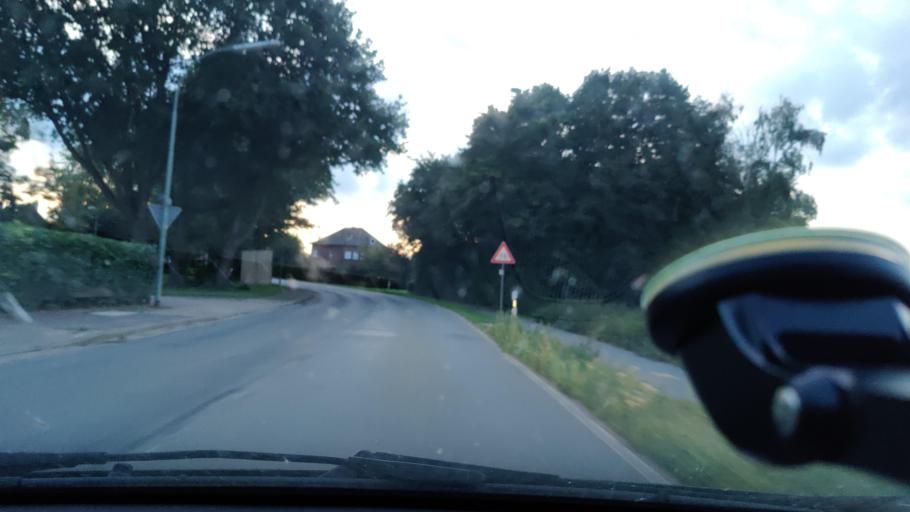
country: DE
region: North Rhine-Westphalia
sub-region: Regierungsbezirk Dusseldorf
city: Goch
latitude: 51.7202
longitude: 6.1783
